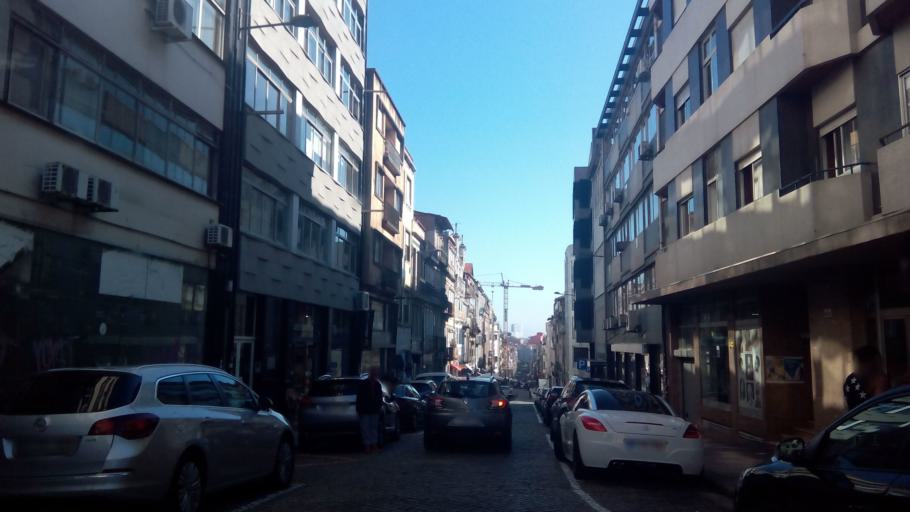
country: PT
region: Porto
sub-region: Porto
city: Porto
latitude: 41.1527
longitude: -8.6047
